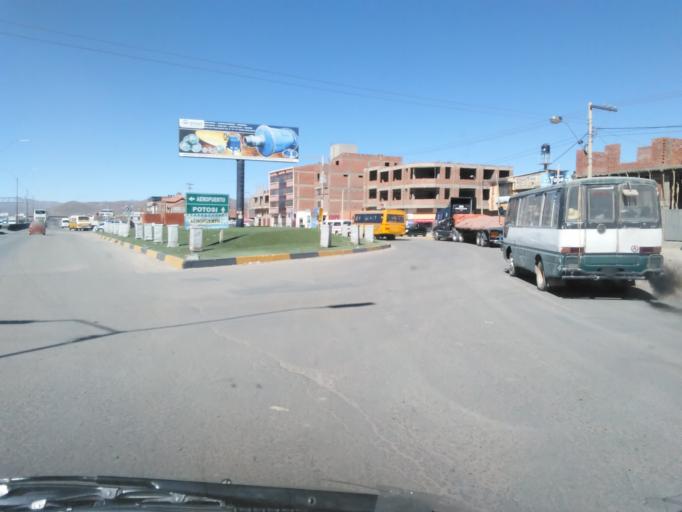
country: BO
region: Oruro
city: Oruro
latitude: -17.9732
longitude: -67.0854
